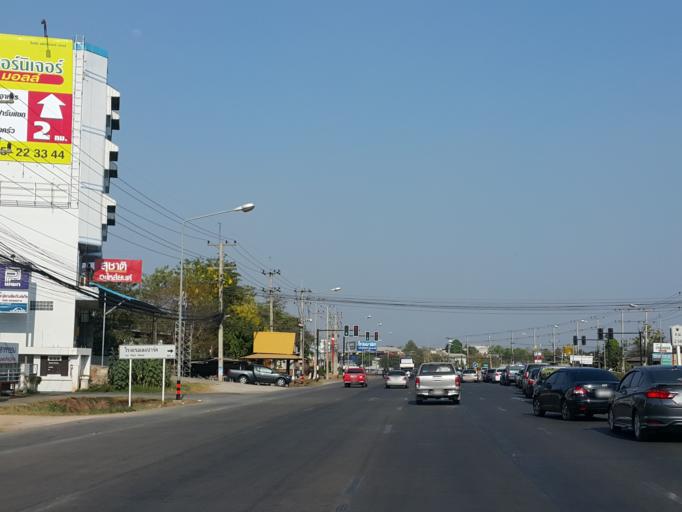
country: TH
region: Phitsanulok
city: Phitsanulok
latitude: 16.8169
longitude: 100.3018
